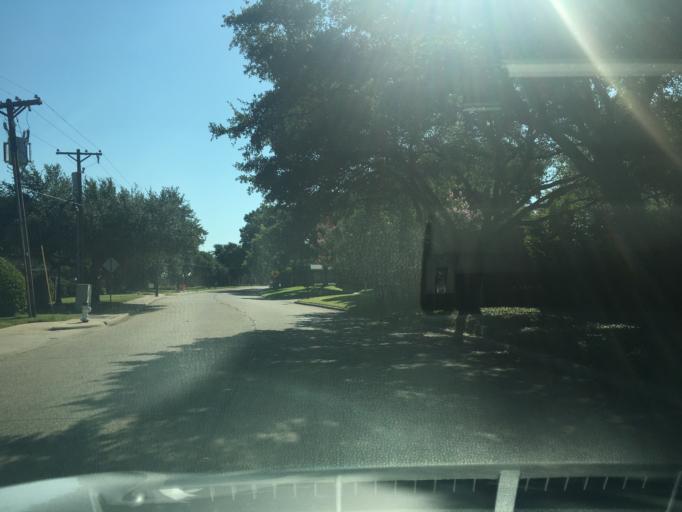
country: US
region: Texas
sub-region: Dallas County
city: Addison
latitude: 32.9512
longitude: -96.8441
